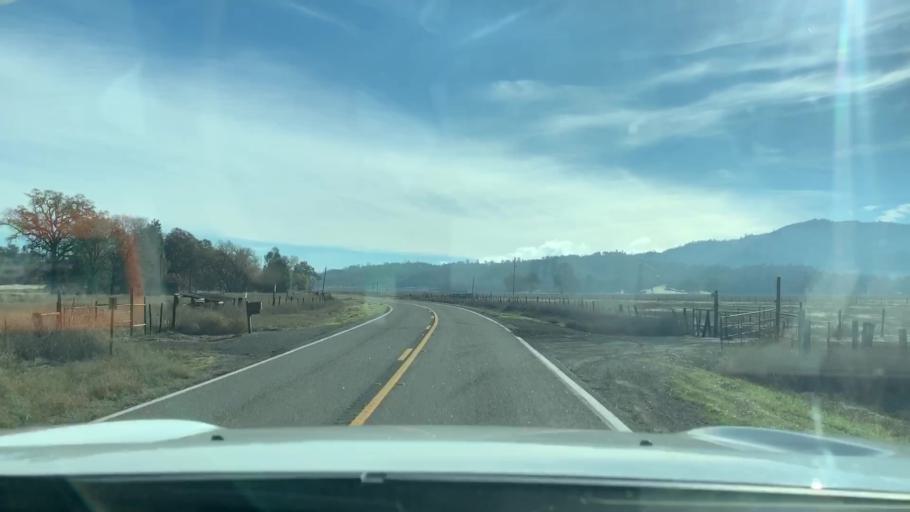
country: US
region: California
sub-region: Fresno County
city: Coalinga
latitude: 36.1782
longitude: -120.6916
